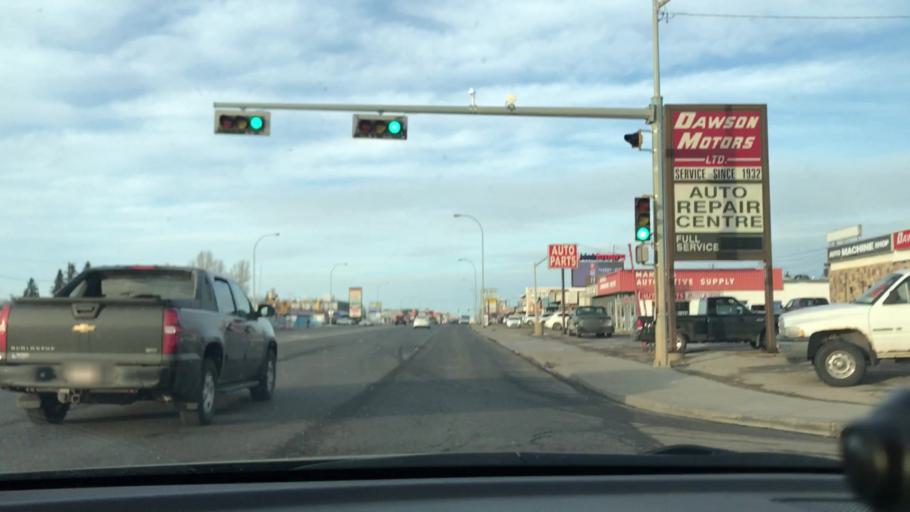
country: CA
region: Alberta
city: Edmonton
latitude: 53.5860
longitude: -113.4918
